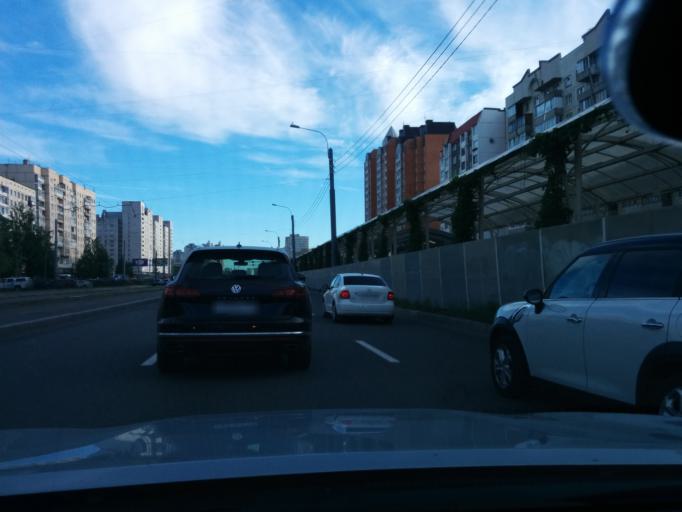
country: RU
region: Leningrad
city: Parnas
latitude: 60.0555
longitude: 30.3367
